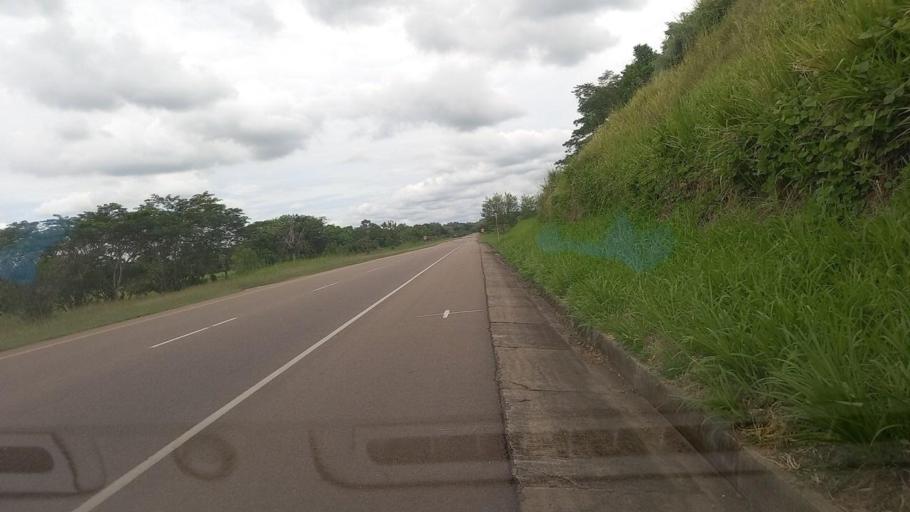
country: CO
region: Antioquia
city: Puerto Triunfo
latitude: 5.8960
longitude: -74.5677
